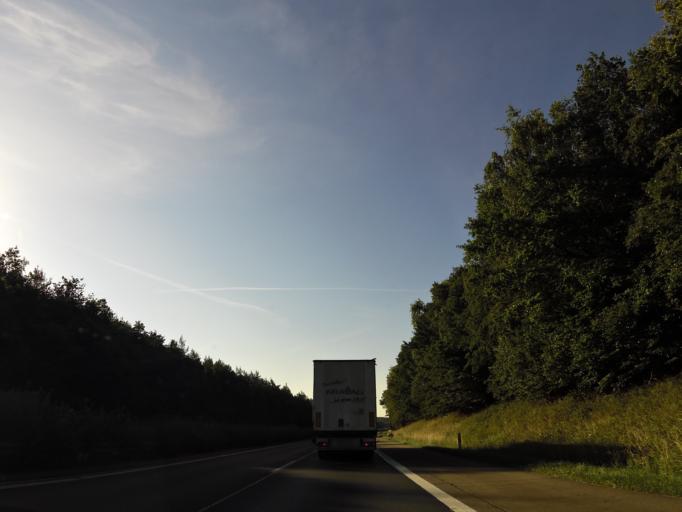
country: DE
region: Bavaria
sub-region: Regierungsbezirk Mittelfranken
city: Hochstadt an der Aisch
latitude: 49.7330
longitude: 10.8128
